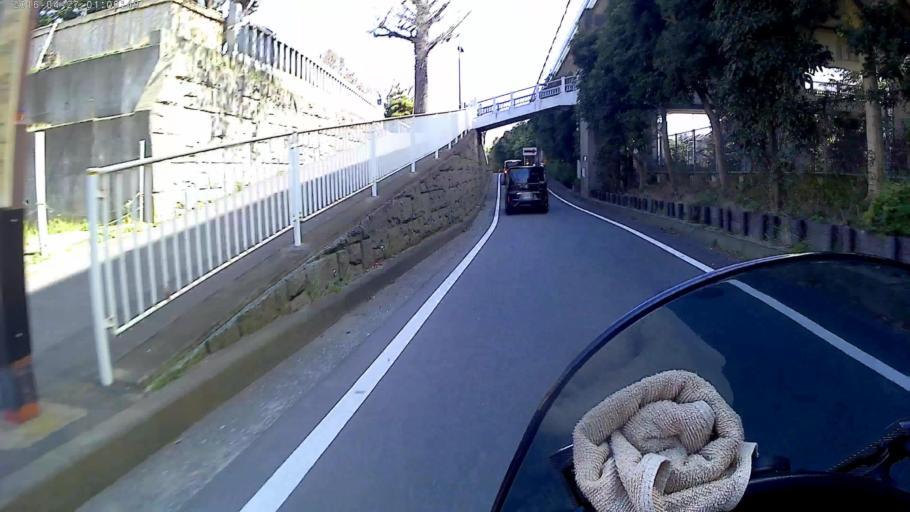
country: JP
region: Kanagawa
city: Chigasaki
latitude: 35.3489
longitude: 139.4207
